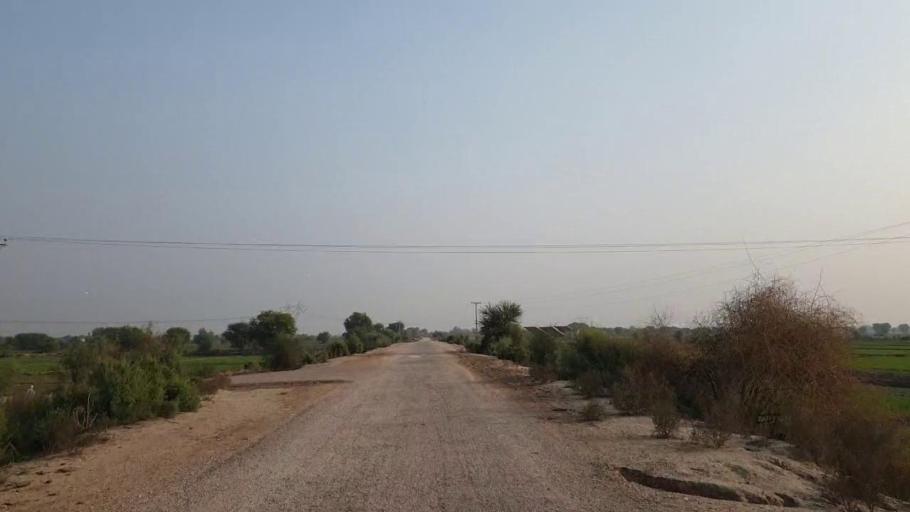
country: PK
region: Sindh
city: Bhan
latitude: 26.4968
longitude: 67.7678
